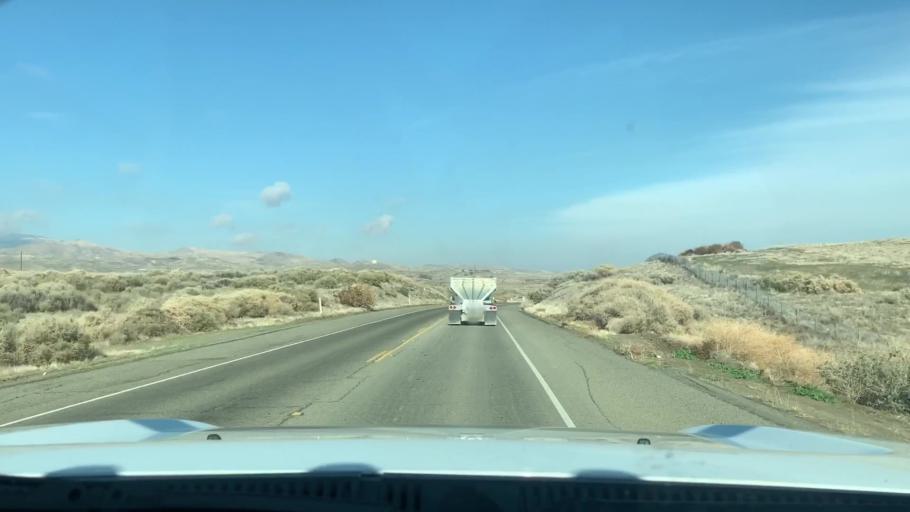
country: US
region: California
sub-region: Fresno County
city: Coalinga
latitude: 36.2262
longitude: -120.3132
